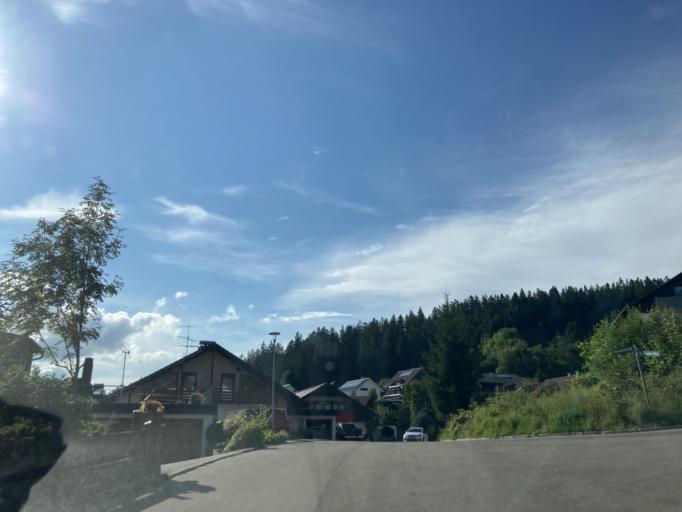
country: DE
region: Baden-Wuerttemberg
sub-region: Freiburg Region
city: Schonach im Schwarzwald
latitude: 48.1445
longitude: 8.2047
